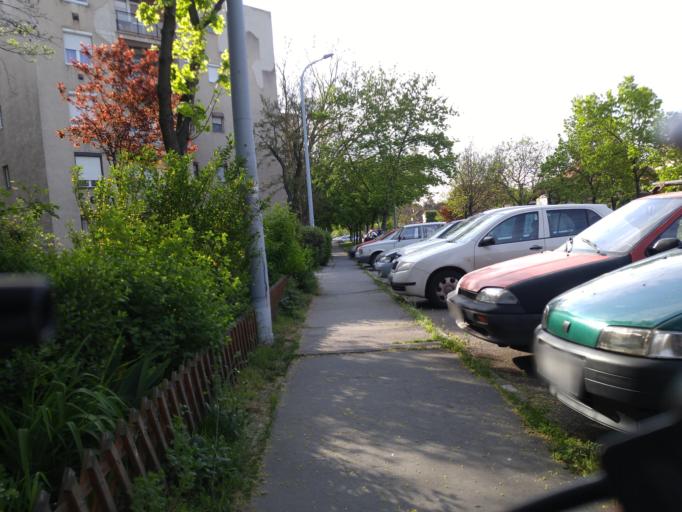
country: HU
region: Budapest
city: Budapest XX. keruelet
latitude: 47.4304
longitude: 19.1246
